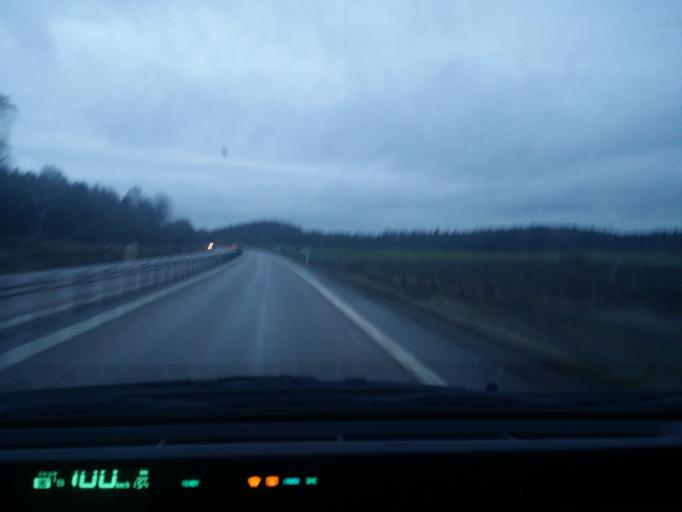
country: SE
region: Soedermanland
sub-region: Eskilstuna Kommun
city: Kvicksund
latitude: 59.4379
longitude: 16.3543
